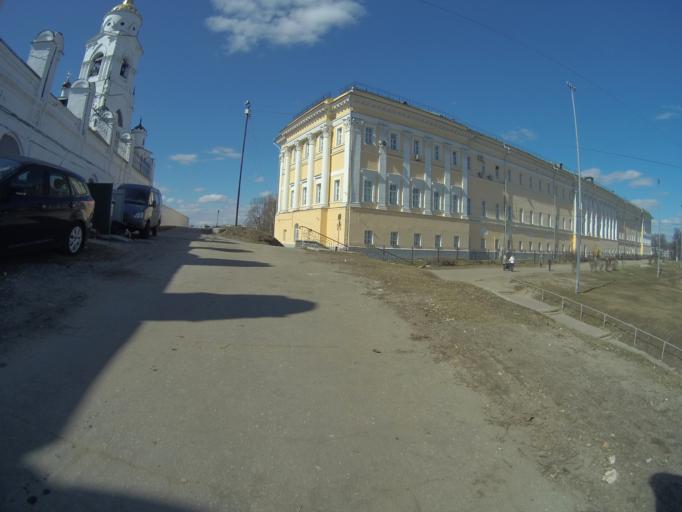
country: RU
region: Vladimir
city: Vladimir
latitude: 56.1275
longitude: 40.4100
